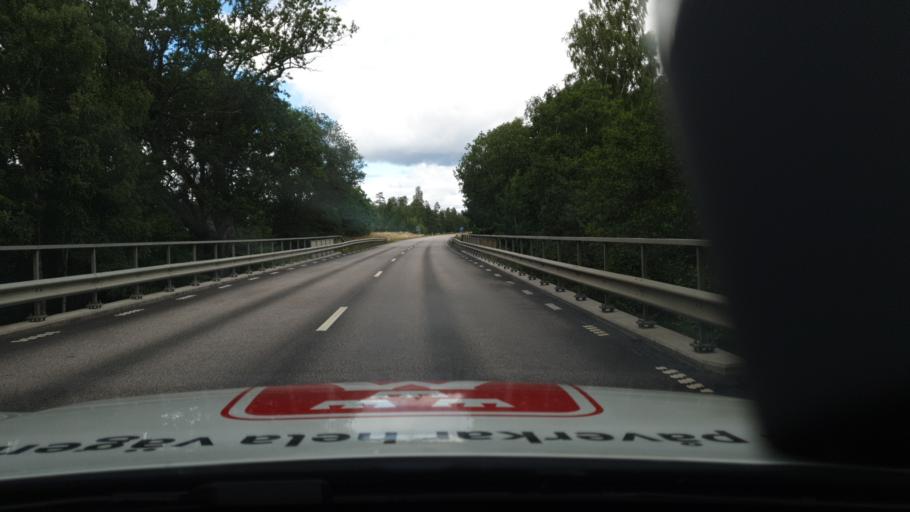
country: SE
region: Vaestra Goetaland
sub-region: Hjo Kommun
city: Hjo
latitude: 58.3081
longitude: 14.2557
